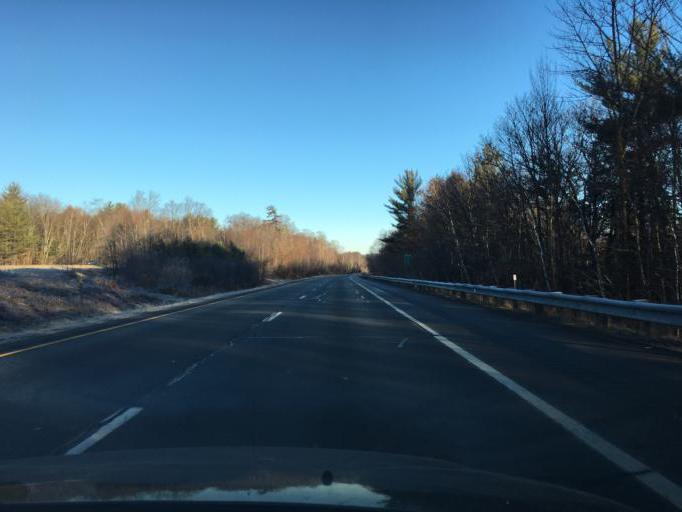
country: US
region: New Hampshire
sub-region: Belknap County
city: Sanbornton
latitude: 43.5474
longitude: -71.6161
